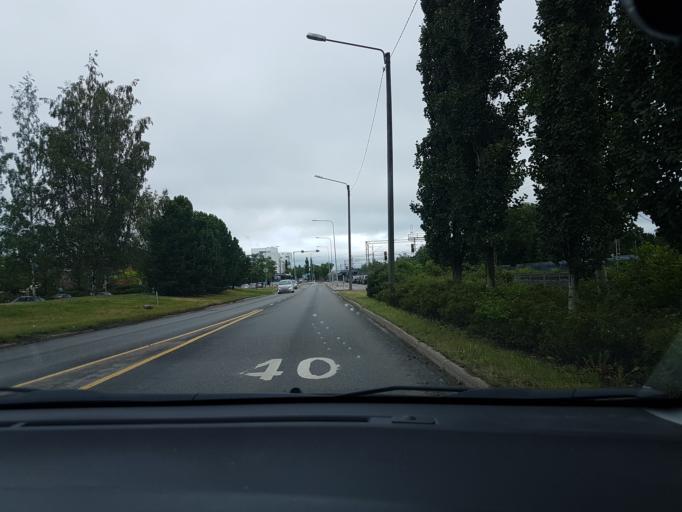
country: FI
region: Uusimaa
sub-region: Helsinki
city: Vantaa
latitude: 60.2732
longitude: 25.0350
